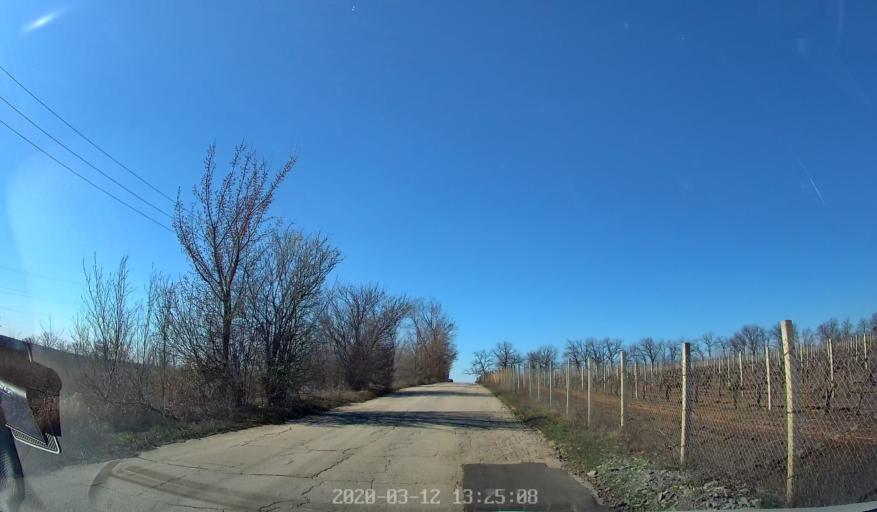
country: MD
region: Laloveni
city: Ialoveni
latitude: 46.9422
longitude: 28.8216
